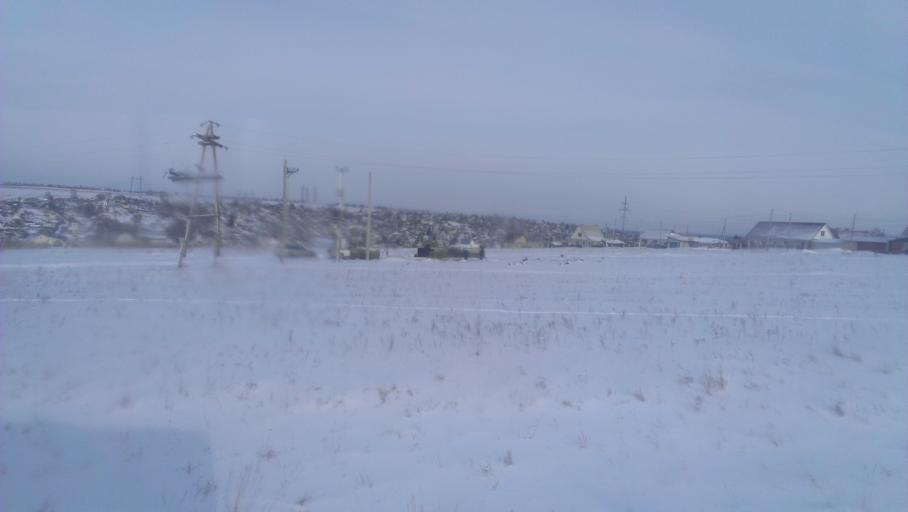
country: RU
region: Altai Krai
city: Gon'ba
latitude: 53.4122
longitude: 83.5581
